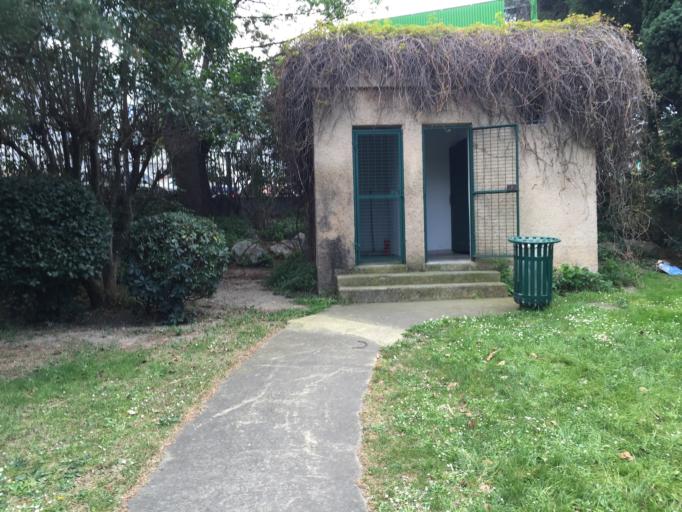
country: FR
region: Provence-Alpes-Cote d'Azur
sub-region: Departement des Bouches-du-Rhone
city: Marseille 09
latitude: 43.2474
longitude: 5.3965
